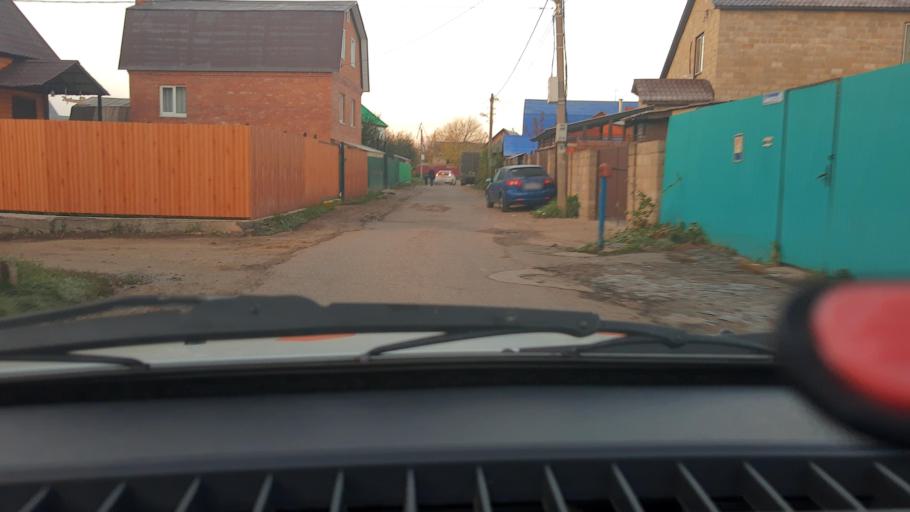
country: RU
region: Bashkortostan
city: Ufa
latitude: 54.7329
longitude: 55.9036
